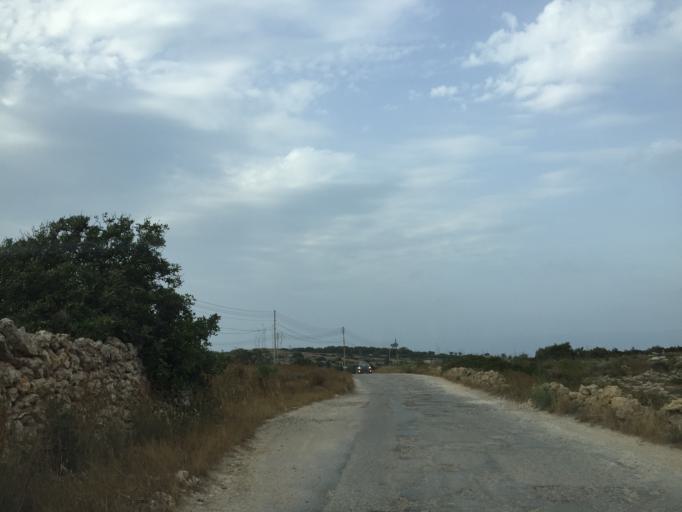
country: MT
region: L-Imgarr
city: Imgarr
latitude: 35.9316
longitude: 14.3865
